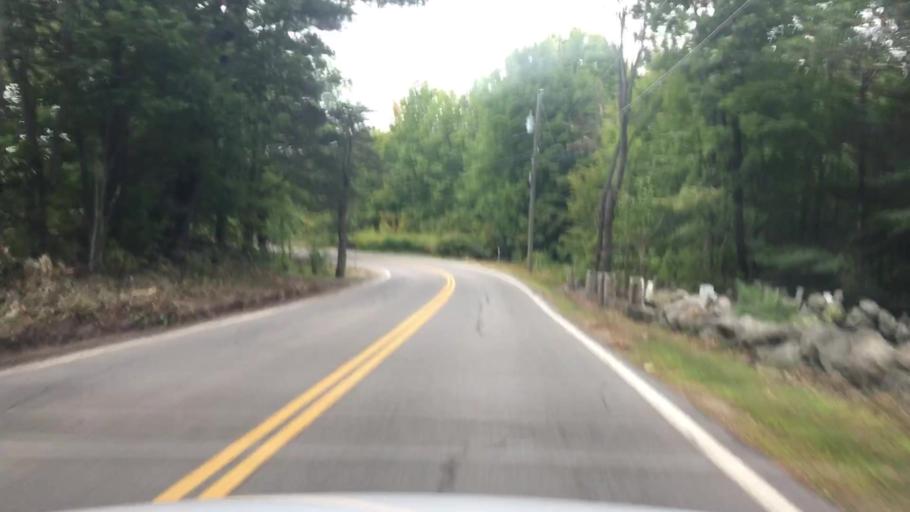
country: US
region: New Hampshire
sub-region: Carroll County
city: Effingham
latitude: 43.7694
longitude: -70.9970
